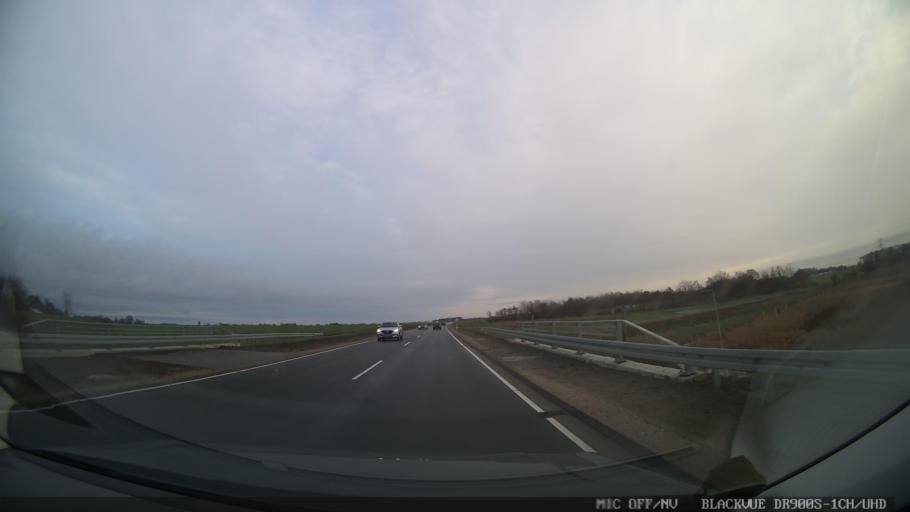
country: DK
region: Central Jutland
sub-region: Arhus Kommune
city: Tranbjerg
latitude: 56.0762
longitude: 10.1286
